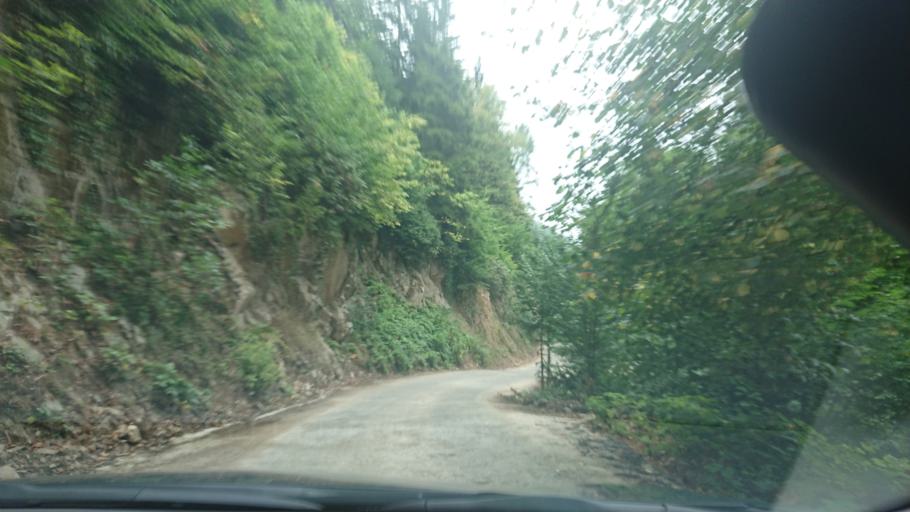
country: TR
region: Gumushane
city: Kurtun
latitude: 40.6711
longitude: 39.0434
